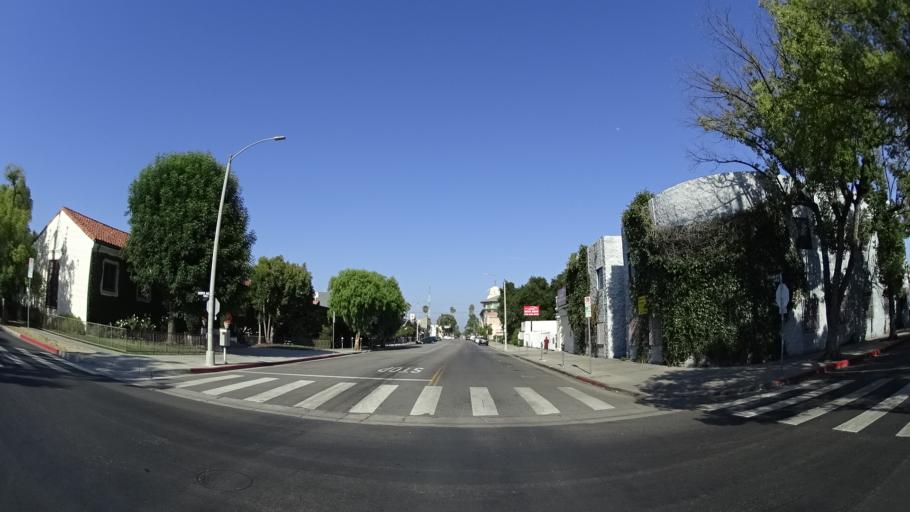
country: US
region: California
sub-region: Los Angeles County
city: Van Nuys
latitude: 34.1846
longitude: -118.4510
